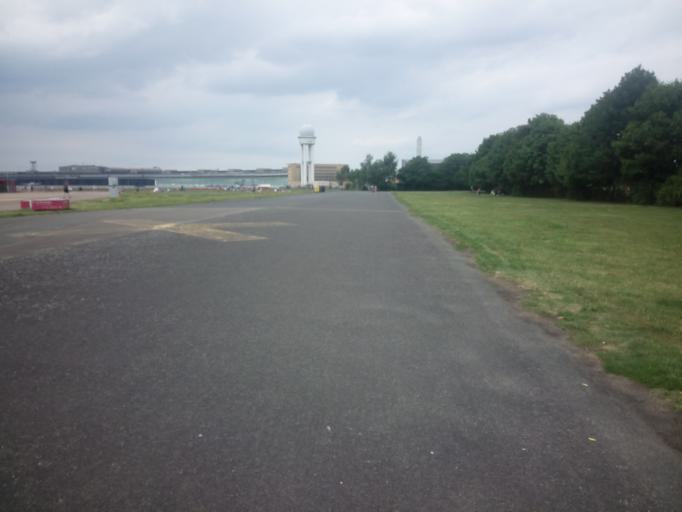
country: DE
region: Berlin
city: Tempelhof Bezirk
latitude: 52.4794
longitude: 13.4073
